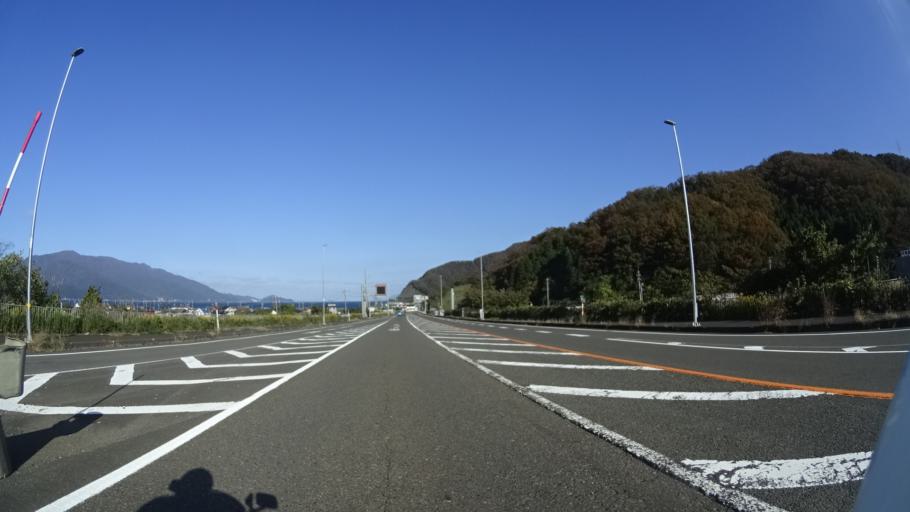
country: JP
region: Fukui
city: Tsuruga
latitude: 35.6772
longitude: 136.0866
